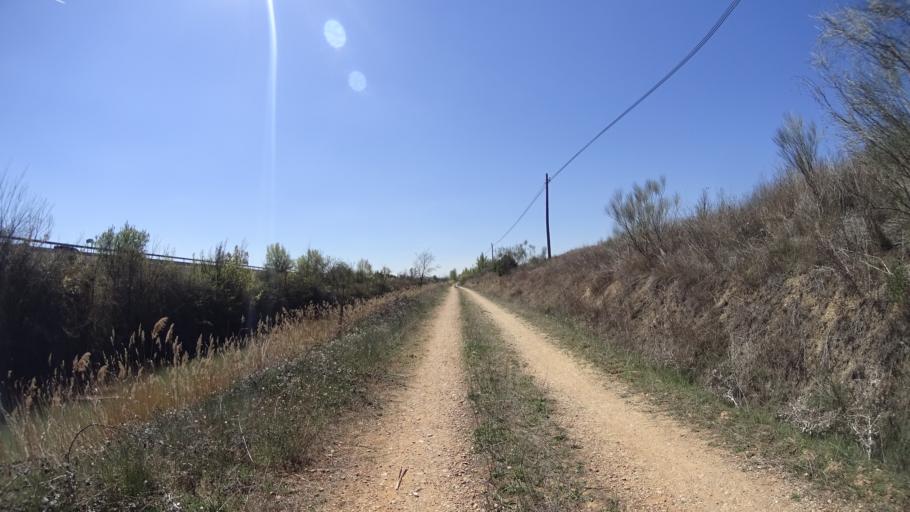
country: ES
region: Castille and Leon
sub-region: Provincia de Palencia
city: Duenas
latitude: 41.8625
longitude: -4.5480
